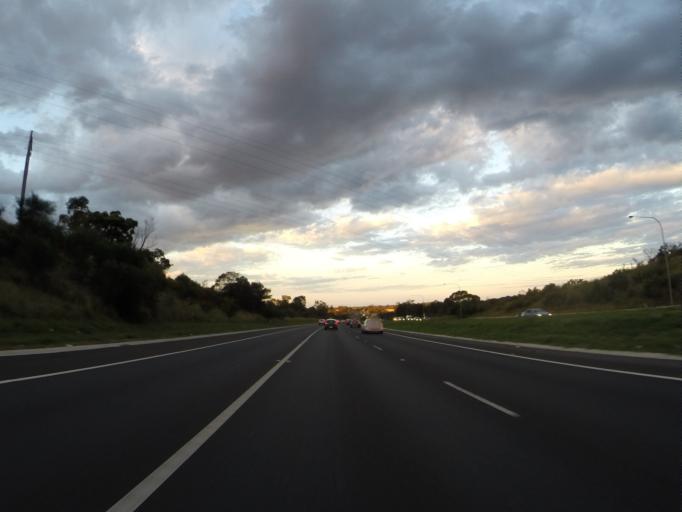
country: AU
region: New South Wales
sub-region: Campbelltown Municipality
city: Campbelltown
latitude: -34.0582
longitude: 150.7920
